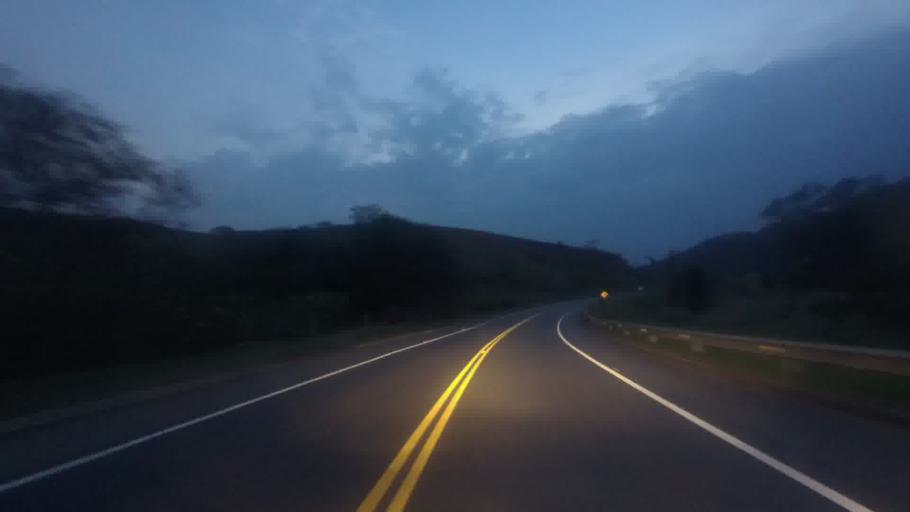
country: BR
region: Rio de Janeiro
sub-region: Sapucaia
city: Sapucaia
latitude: -21.9438
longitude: -42.8300
